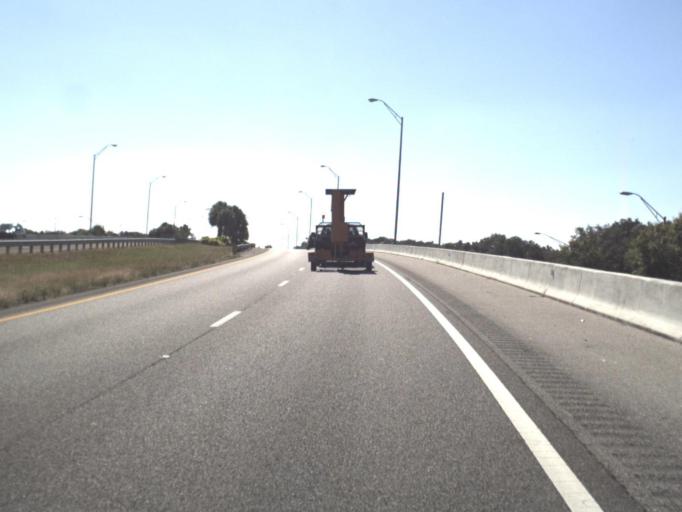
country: US
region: Florida
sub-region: Hillsborough County
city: Citrus Park
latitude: 28.0806
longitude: -82.5619
